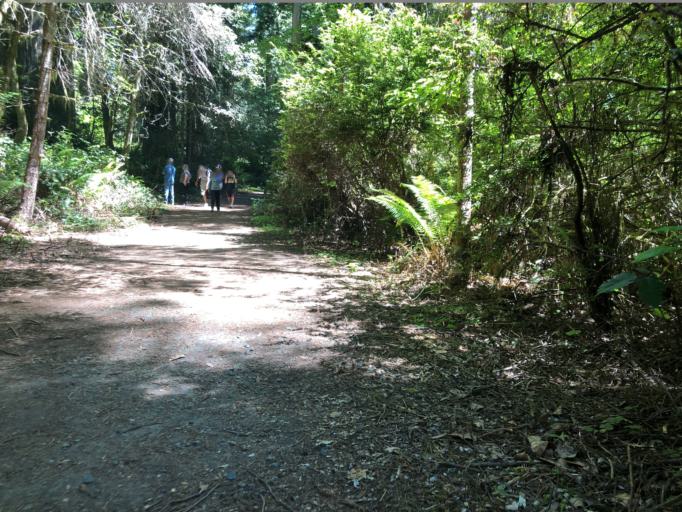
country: US
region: California
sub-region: Humboldt County
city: Westhaven-Moonstone
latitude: 41.3070
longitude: -124.0221
